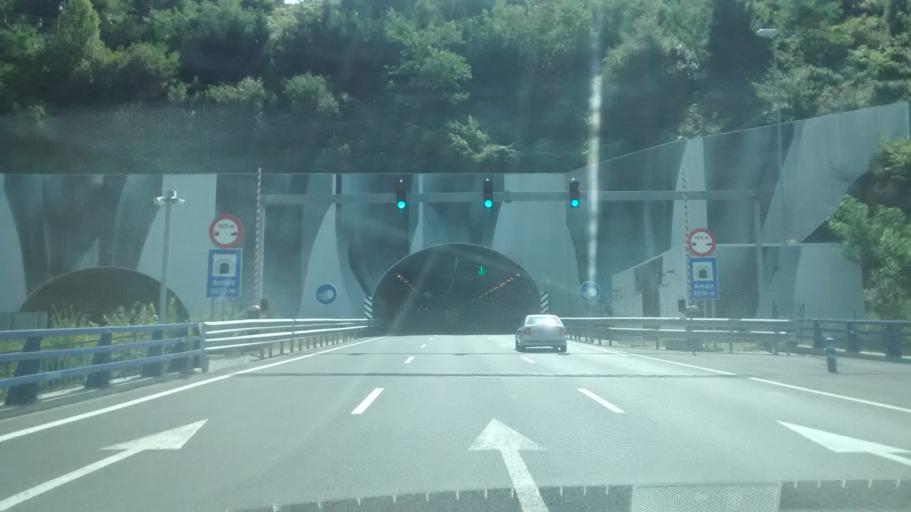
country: ES
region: Basque Country
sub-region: Bizkaia
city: Alonsotegi
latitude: 43.2507
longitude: -2.9740
